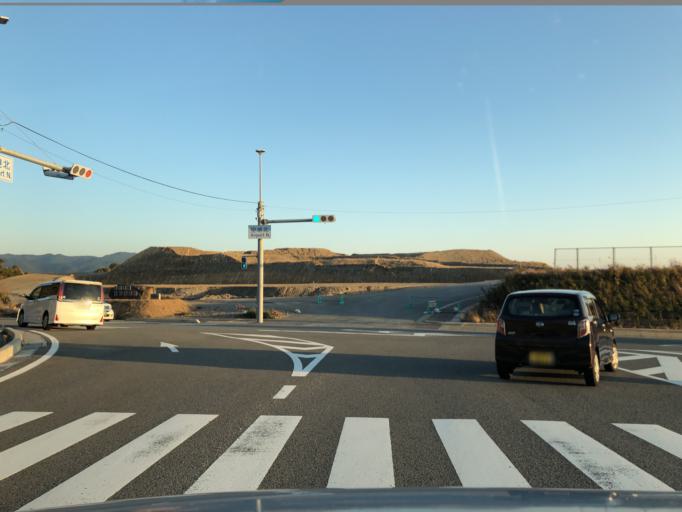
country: JP
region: Wakayama
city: Tanabe
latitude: 33.6667
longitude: 135.3636
